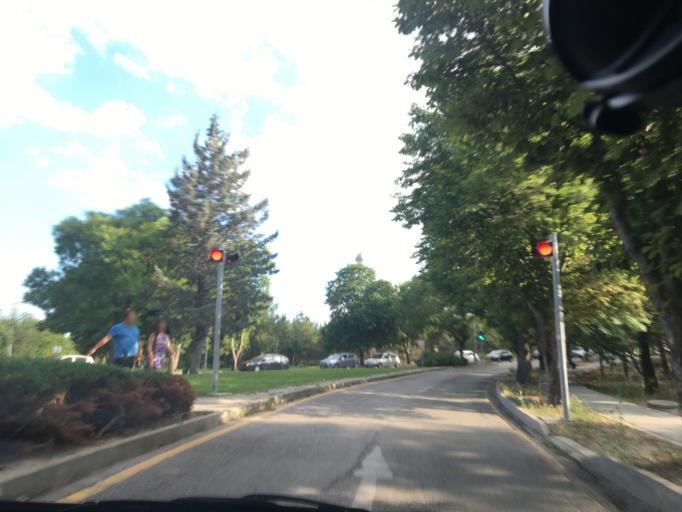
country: TR
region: Ankara
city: Ankara
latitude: 39.9016
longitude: 32.7831
